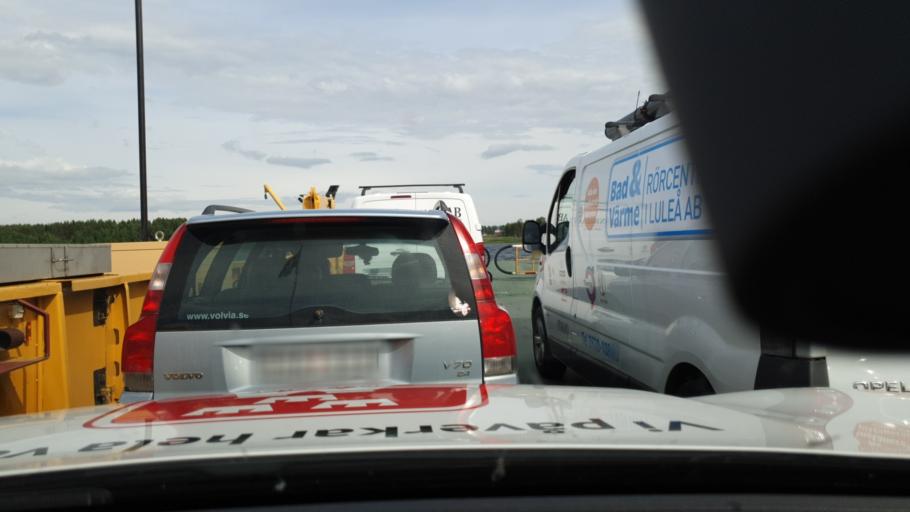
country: SE
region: Norrbotten
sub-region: Lulea Kommun
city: Sodra Sunderbyn
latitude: 65.6800
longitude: 21.8215
